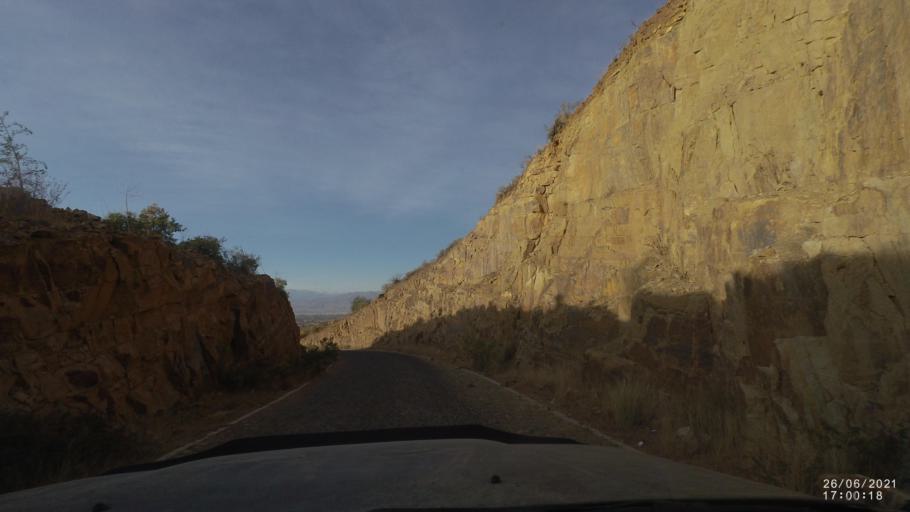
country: BO
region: Cochabamba
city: Cliza
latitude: -17.6610
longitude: -65.9077
